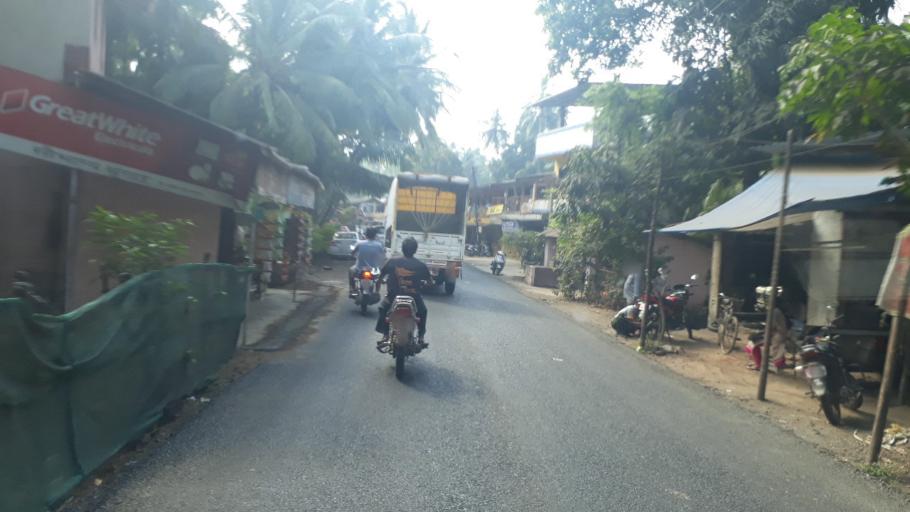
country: IN
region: Maharashtra
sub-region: Raigarh
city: Revadanda
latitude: 18.5815
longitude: 72.9245
